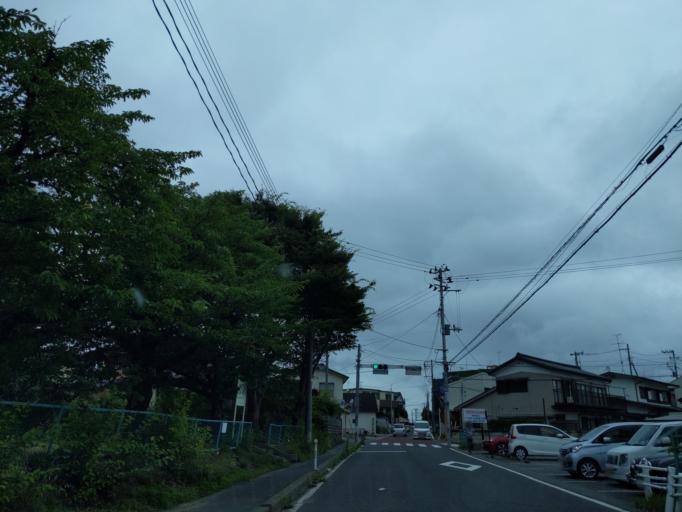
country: JP
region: Fukushima
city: Koriyama
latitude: 37.3895
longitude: 140.3522
